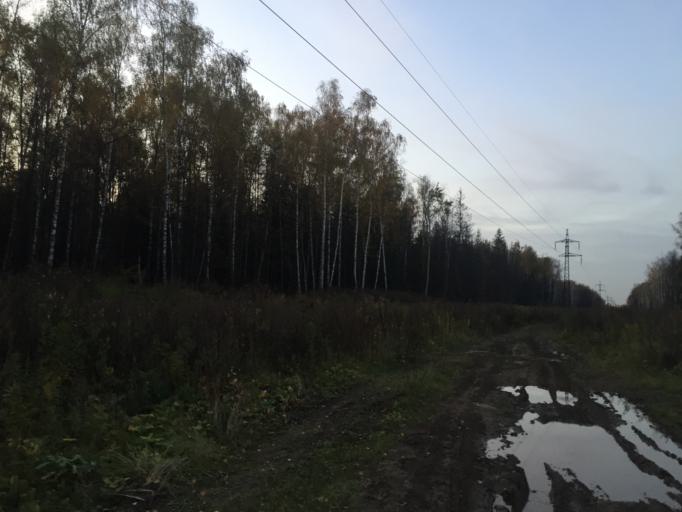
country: RU
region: Moskovskaya
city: Druzhba
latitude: 55.8689
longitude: 37.7676
